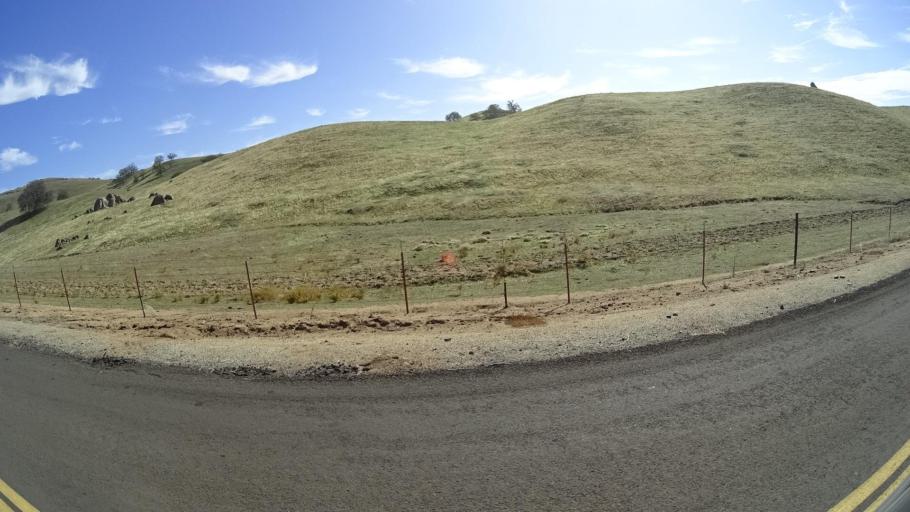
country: US
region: California
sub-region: Tulare County
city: Richgrove
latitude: 35.6845
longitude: -118.8816
